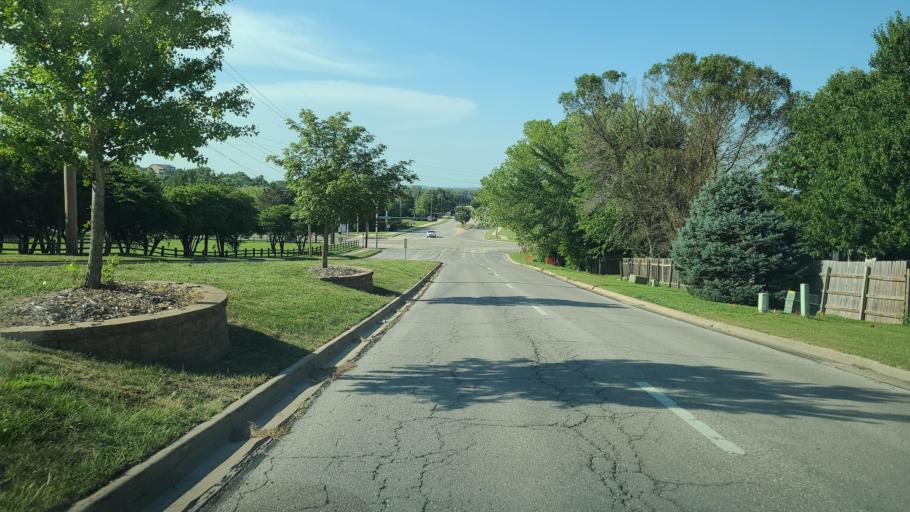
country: US
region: Kansas
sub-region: Douglas County
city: Lawrence
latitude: 38.9847
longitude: -95.2789
